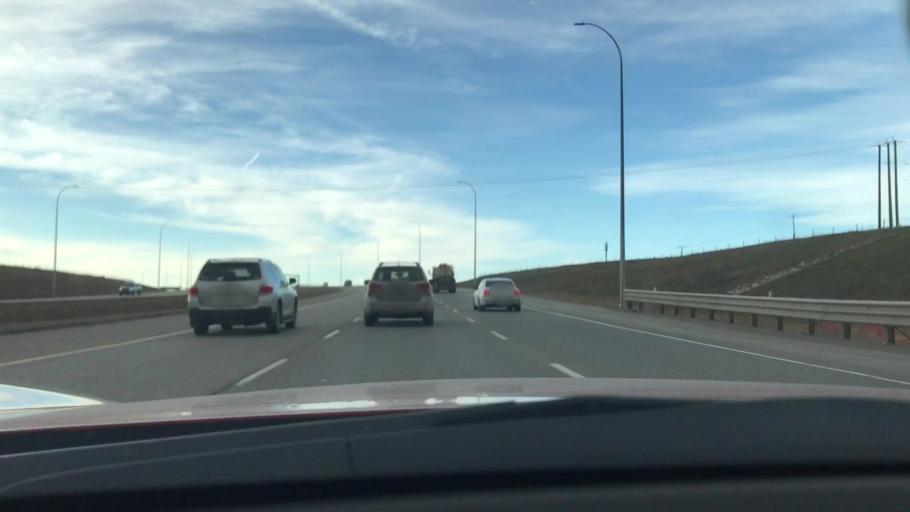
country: CA
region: Alberta
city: Calgary
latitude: 51.1509
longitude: -114.1869
